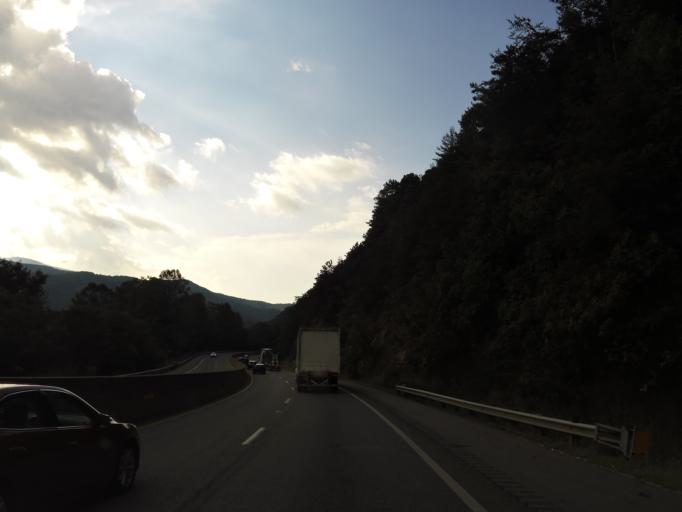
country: US
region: North Carolina
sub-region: Haywood County
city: Cove Creek
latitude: 35.6904
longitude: -83.0345
